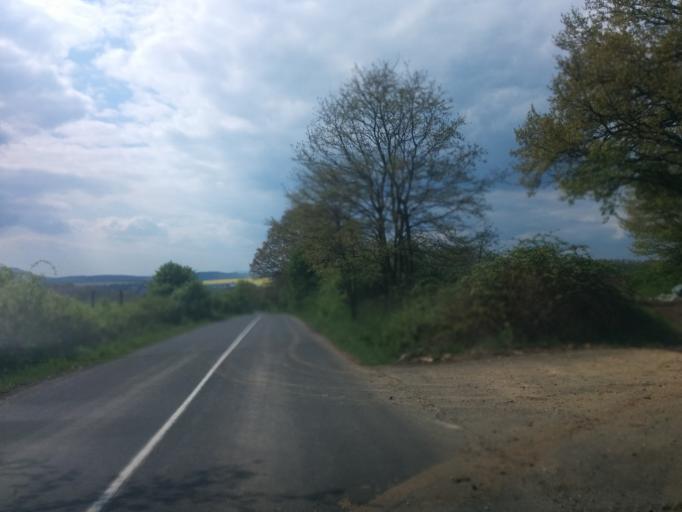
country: HU
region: Pest
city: Acsa
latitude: 47.8435
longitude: 19.3258
